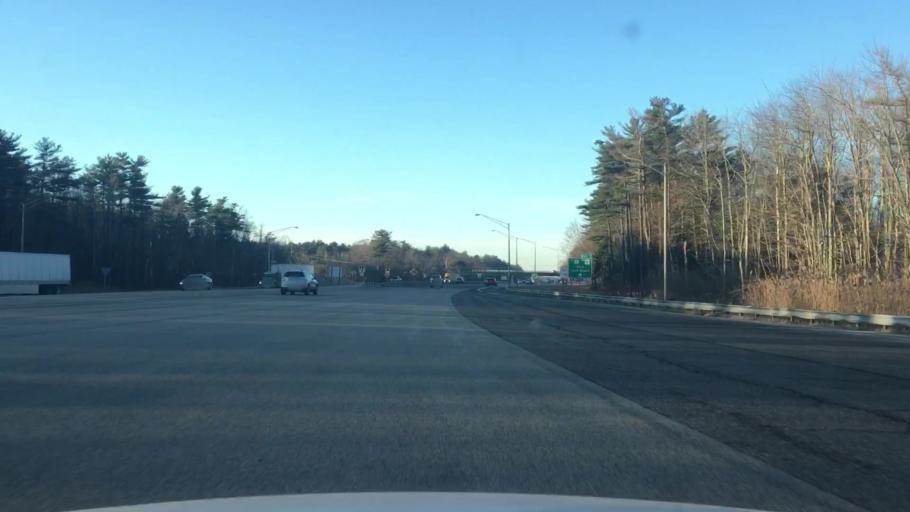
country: US
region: Maine
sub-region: York County
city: York Harbor
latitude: 43.1594
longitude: -70.6606
